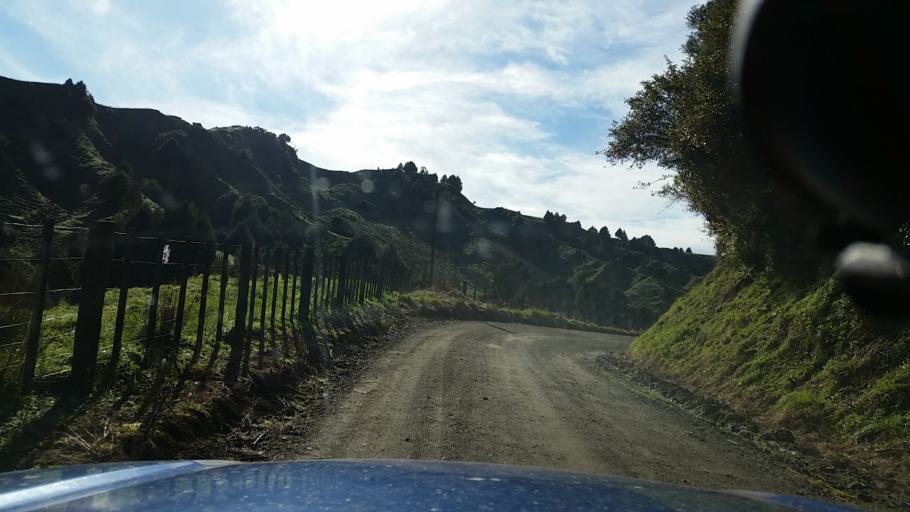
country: NZ
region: Taranaki
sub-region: New Plymouth District
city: Waitara
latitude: -39.0517
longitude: 174.7551
